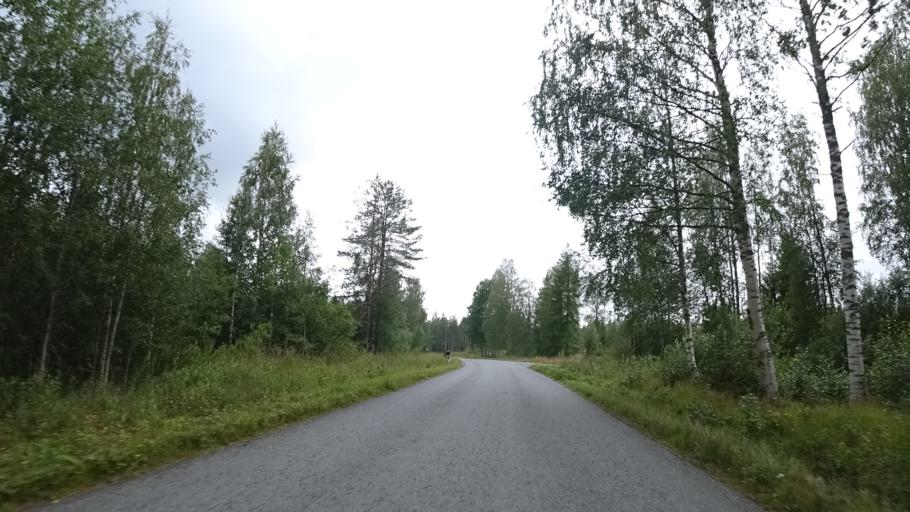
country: FI
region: North Karelia
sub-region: Joensuu
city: Ilomantsi
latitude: 62.9419
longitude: 31.2909
